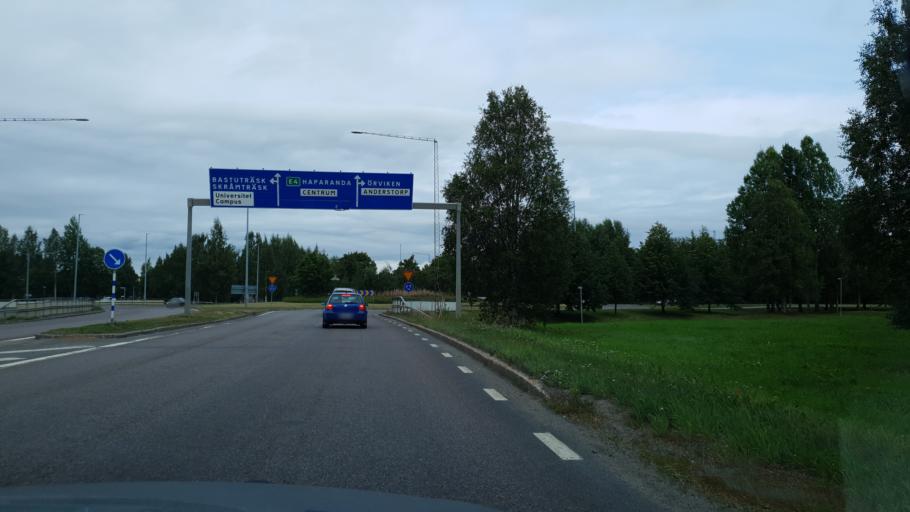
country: SE
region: Vaesterbotten
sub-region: Skelleftea Kommun
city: Skelleftea
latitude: 64.7423
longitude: 20.9618
